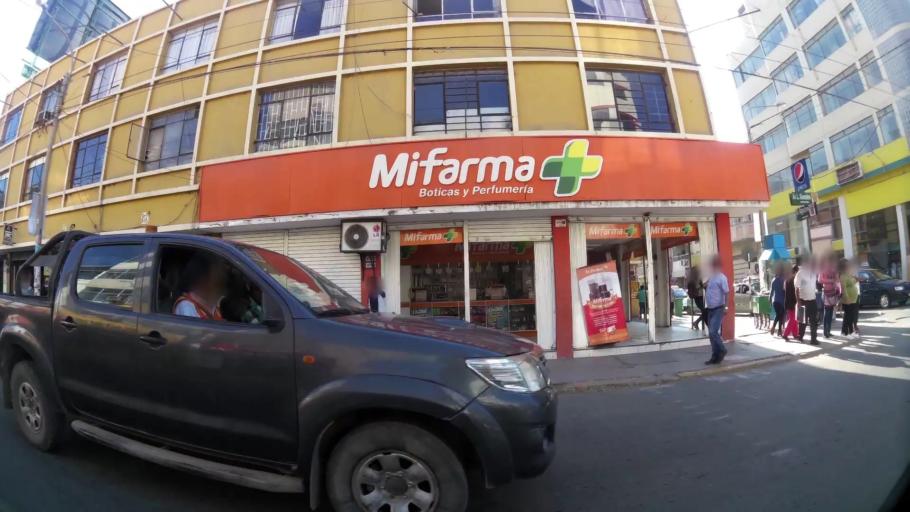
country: PE
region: Lambayeque
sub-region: Provincia de Chiclayo
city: Chiclayo
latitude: -6.7716
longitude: -79.8422
